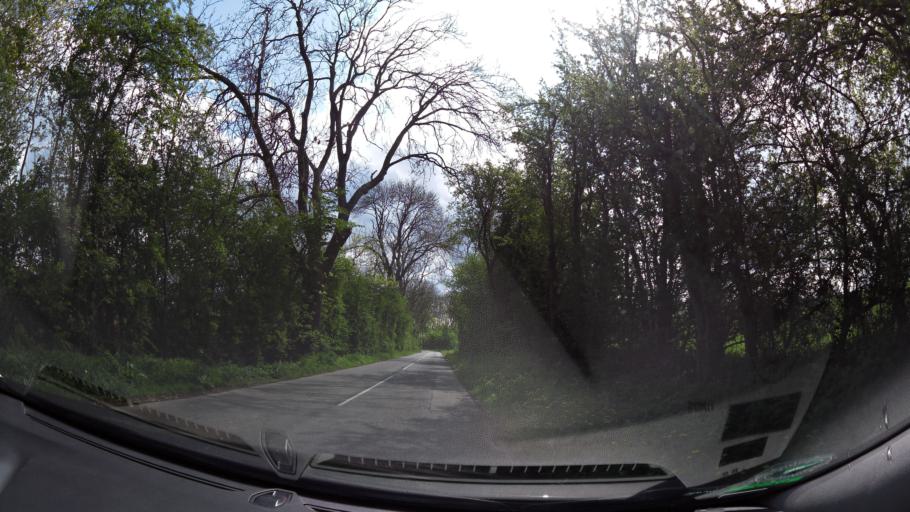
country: DK
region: South Denmark
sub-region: Svendborg Kommune
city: Thuro By
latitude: 55.1409
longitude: 10.7643
